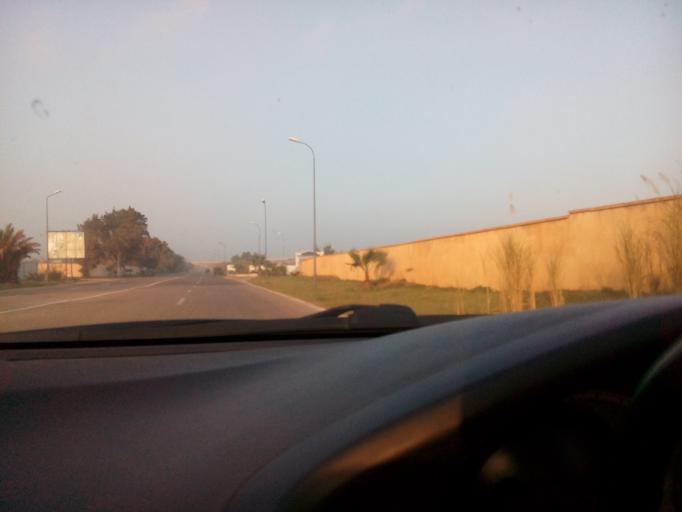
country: DZ
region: Oran
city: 'Ain el Turk
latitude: 35.7126
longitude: -0.8590
